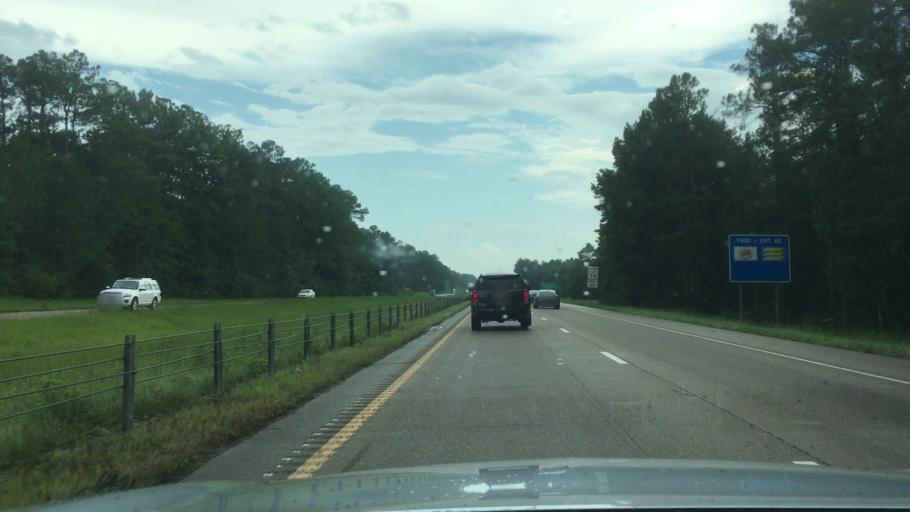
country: US
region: Mississippi
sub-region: Lamar County
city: West Hattiesburg
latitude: 31.2507
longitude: -89.3305
